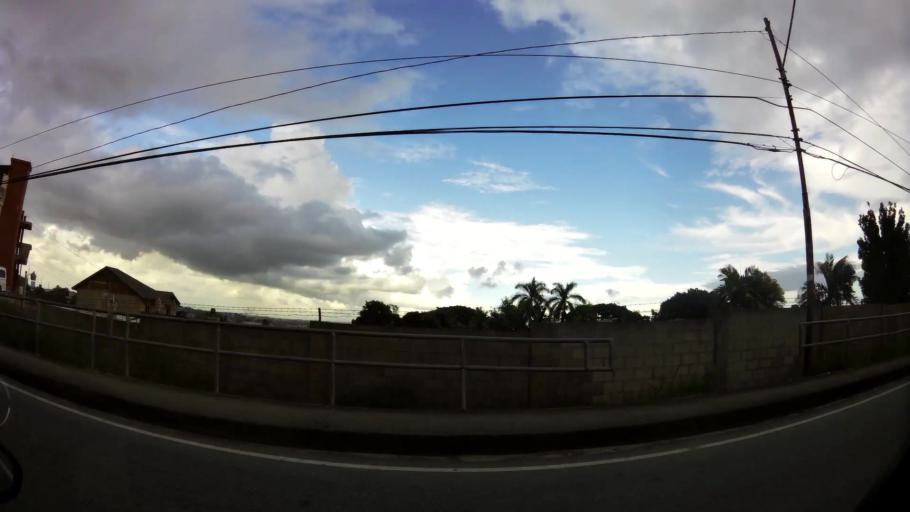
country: TT
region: Penal/Debe
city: Debe
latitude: 10.2447
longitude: -61.4551
